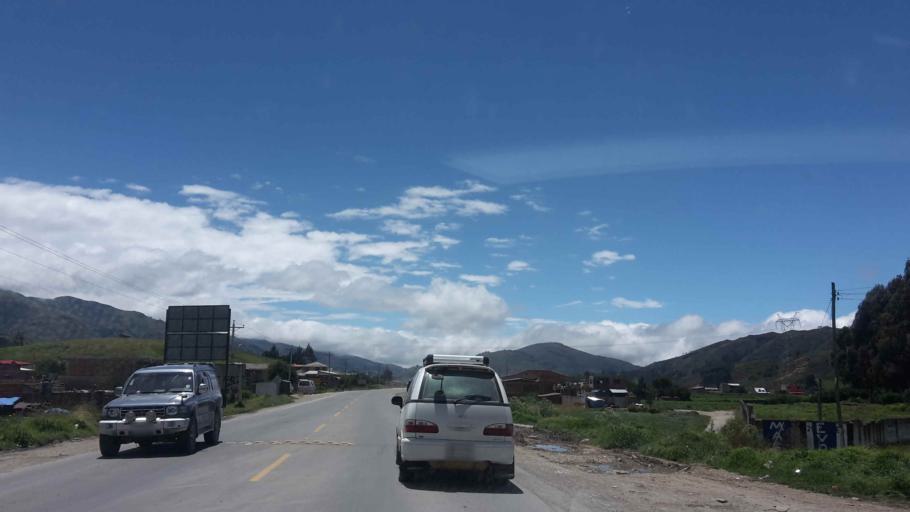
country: BO
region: Cochabamba
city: Colomi
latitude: -17.3298
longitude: -65.8726
